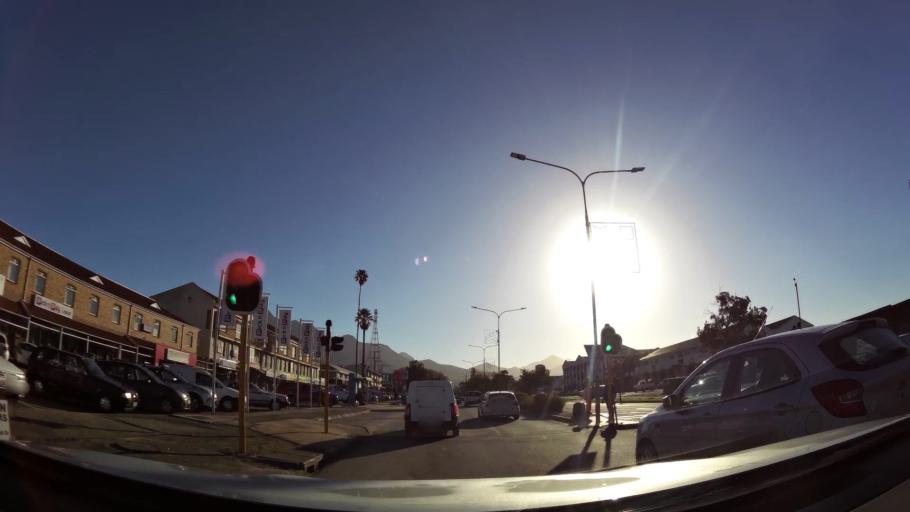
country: ZA
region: Western Cape
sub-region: Eden District Municipality
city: George
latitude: -33.9636
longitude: 22.4528
